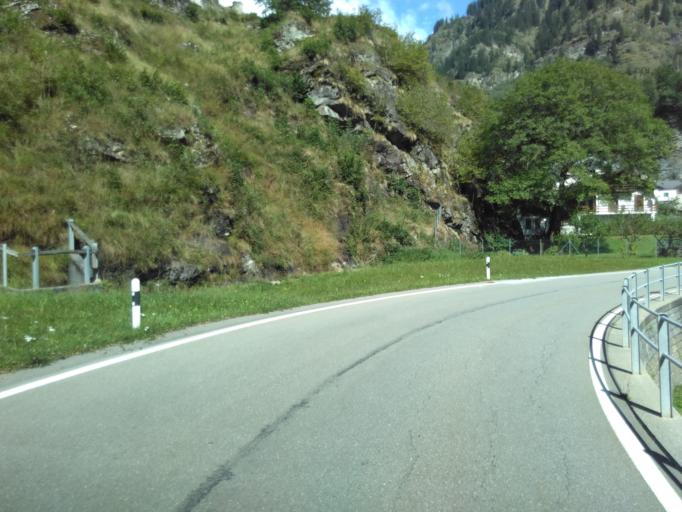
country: CH
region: Grisons
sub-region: Moesa District
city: Cauco
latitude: 46.3300
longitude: 9.1177
